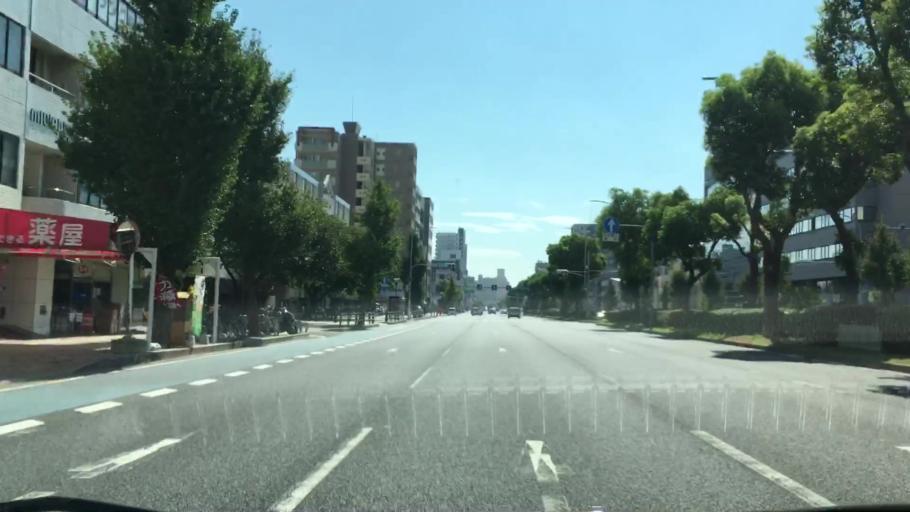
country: JP
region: Hyogo
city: Kobe
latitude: 34.6744
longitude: 135.1667
